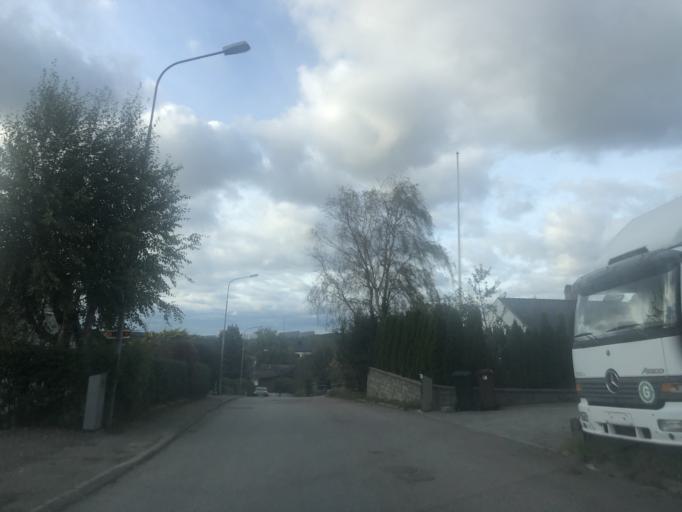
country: SE
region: Vaestra Goetaland
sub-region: Goteborg
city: Majorna
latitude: 57.6362
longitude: 11.9484
